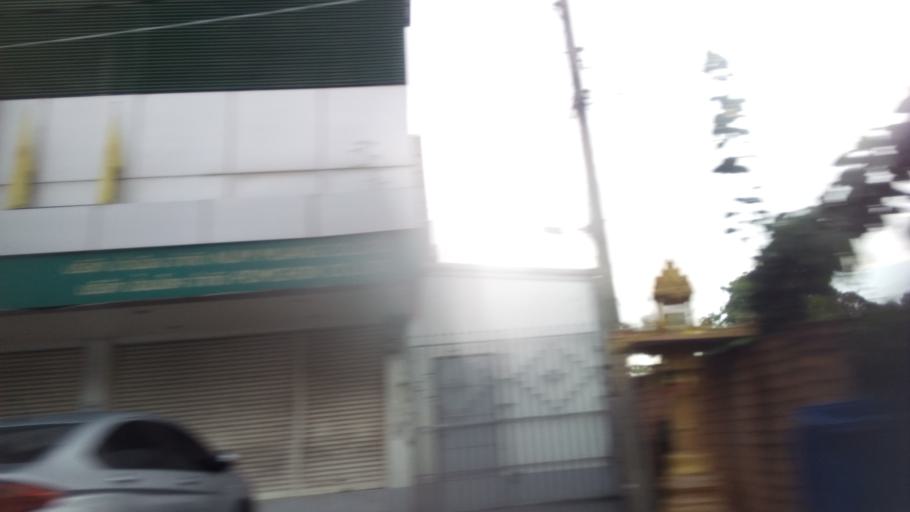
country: TH
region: Phra Nakhon Si Ayutthaya
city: Phra Nakhon Si Ayutthaya
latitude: 14.3570
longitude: 100.5488
